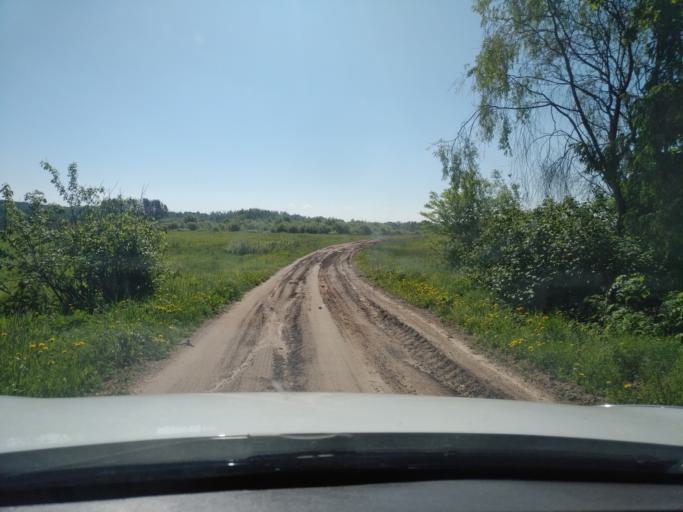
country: LT
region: Panevezys
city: Rokiskis
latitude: 55.7484
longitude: 25.6104
